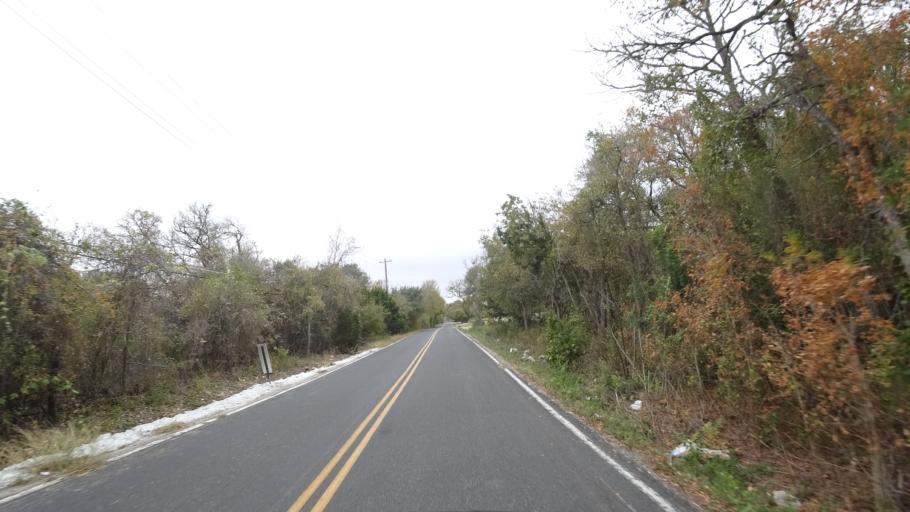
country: US
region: Texas
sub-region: Travis County
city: Manchaca
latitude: 30.1444
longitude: -97.8470
